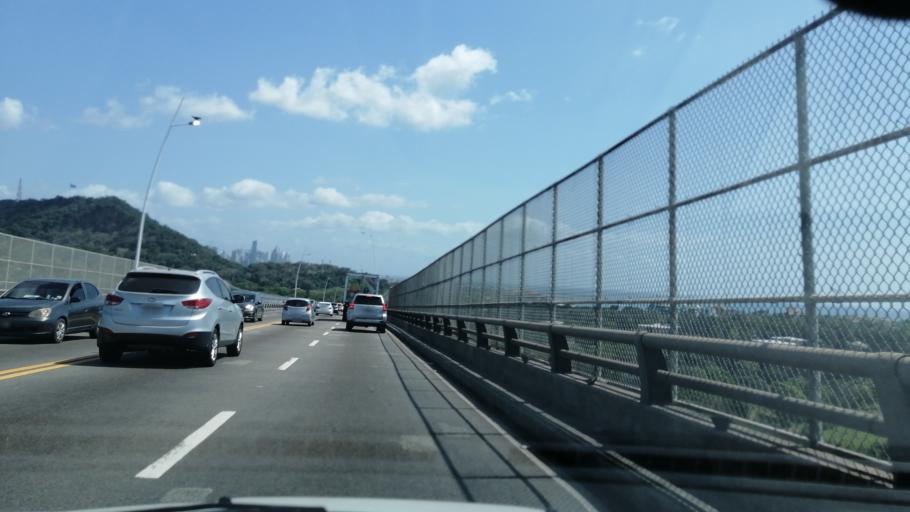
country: PA
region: Panama
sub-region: Distrito de Panama
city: Ancon
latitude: 8.9441
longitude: -79.5627
